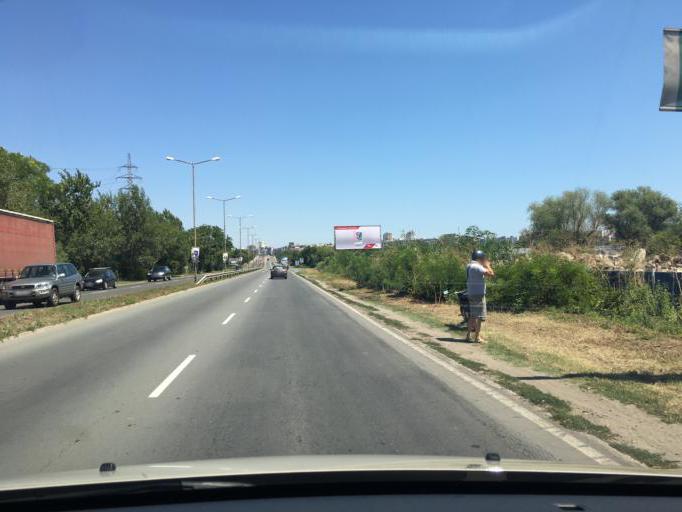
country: BG
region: Burgas
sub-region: Obshtina Burgas
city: Burgas
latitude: 42.4944
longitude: 27.4515
